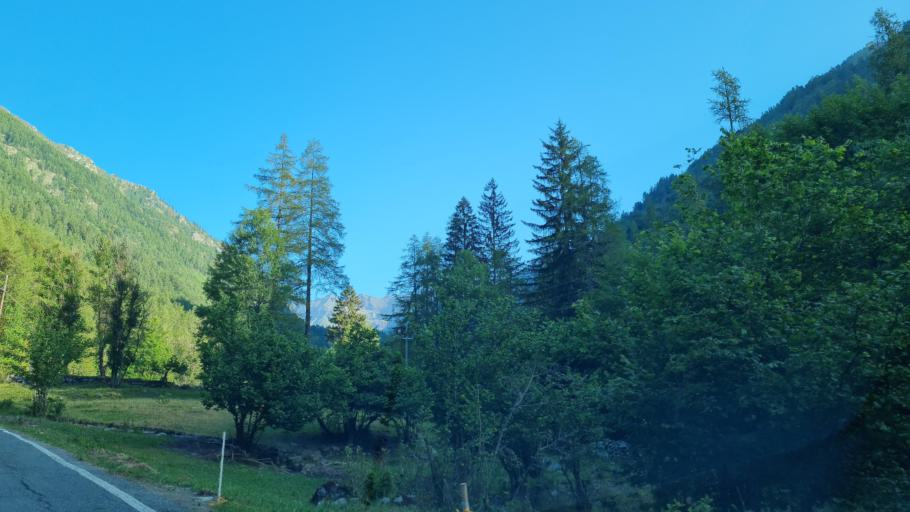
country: IT
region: Piedmont
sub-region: Provincia di Torino
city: Valprato Soana
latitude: 45.5252
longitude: 7.5486
